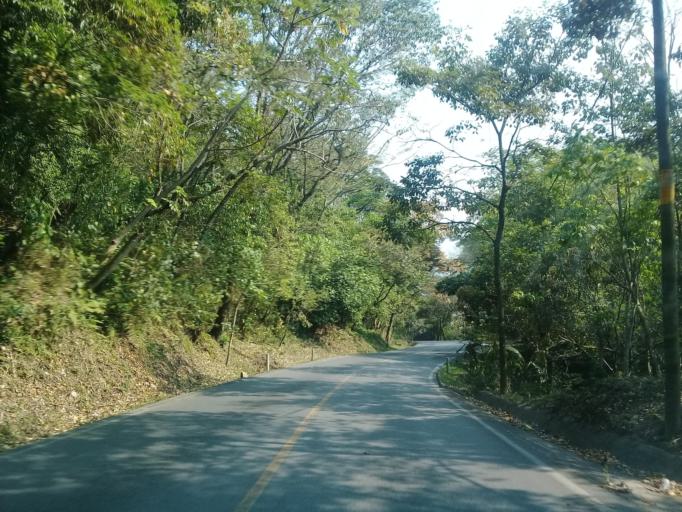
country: MX
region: Veracruz
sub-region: Ixtaczoquitlan
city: Campo Chico
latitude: 18.8429
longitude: -97.0286
